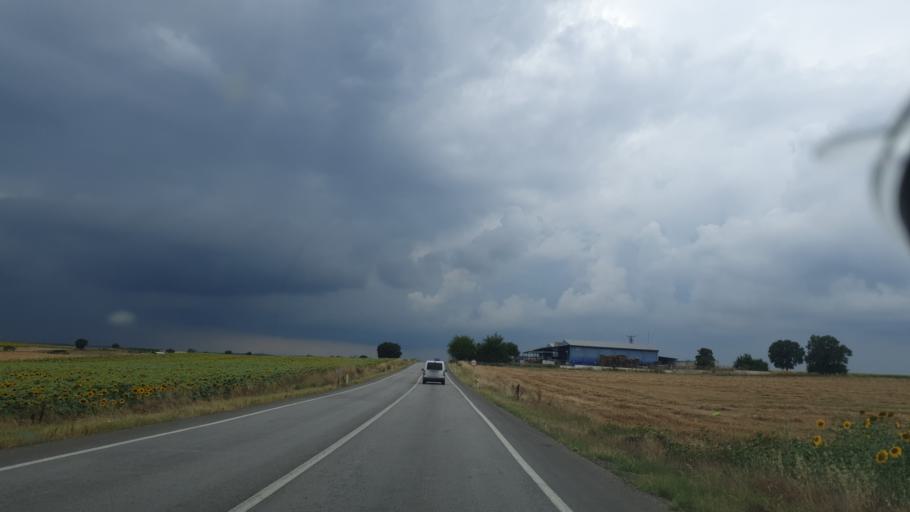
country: TR
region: Tekirdag
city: Hayrabolu
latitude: 41.2186
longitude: 27.0817
